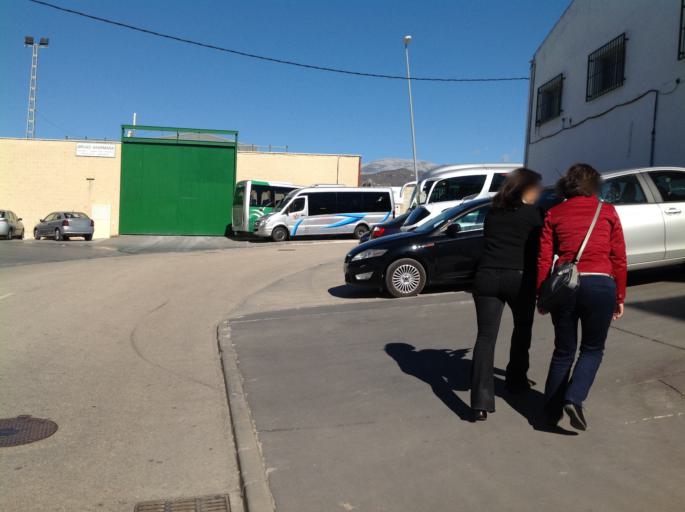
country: ES
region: Andalusia
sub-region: Provincia de Malaga
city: Velez-Malaga
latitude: 36.7663
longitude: -4.0926
